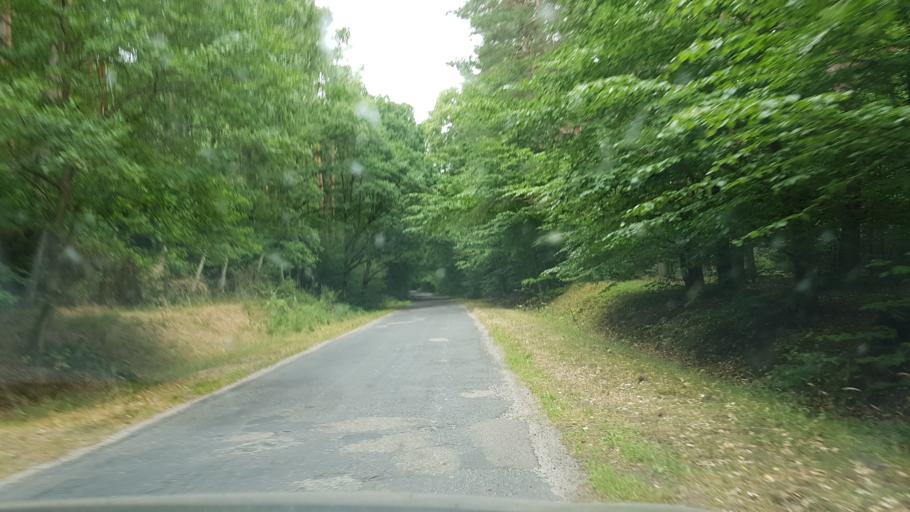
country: PL
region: West Pomeranian Voivodeship
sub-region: Powiat kamienski
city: Miedzyzdroje
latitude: 53.9365
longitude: 14.5403
